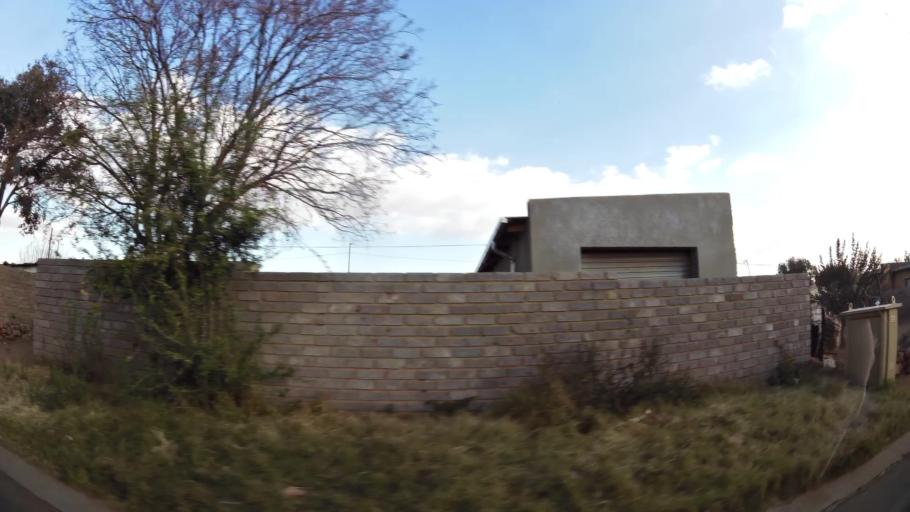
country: ZA
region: Gauteng
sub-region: West Rand District Municipality
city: Krugersdorp
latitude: -26.0730
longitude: 27.7592
